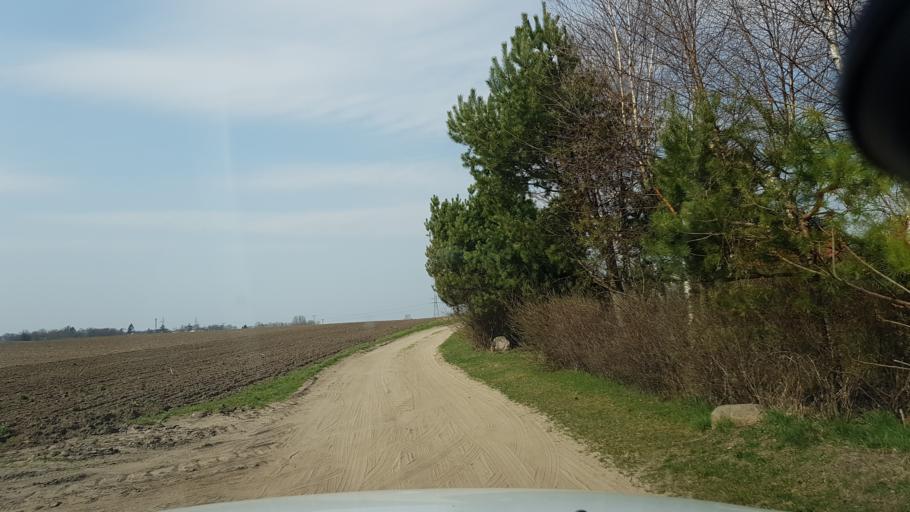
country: PL
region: West Pomeranian Voivodeship
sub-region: Powiat stargardzki
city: Stargard Szczecinski
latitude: 53.3391
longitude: 15.0759
